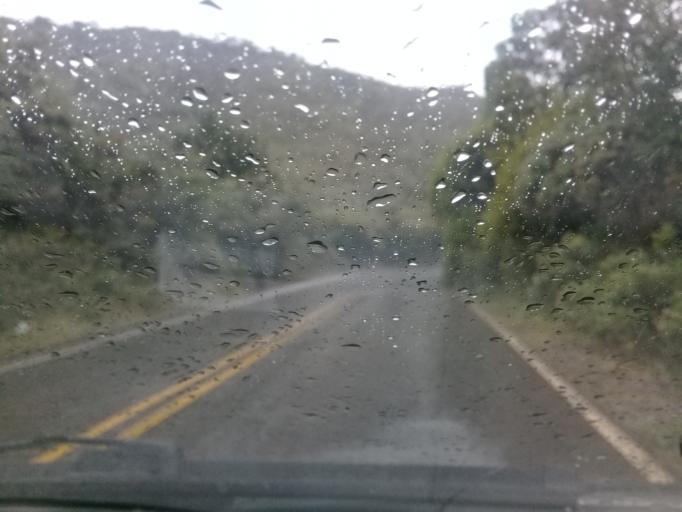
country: CO
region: Cundinamarca
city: Guasca
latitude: 4.8429
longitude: -73.8299
